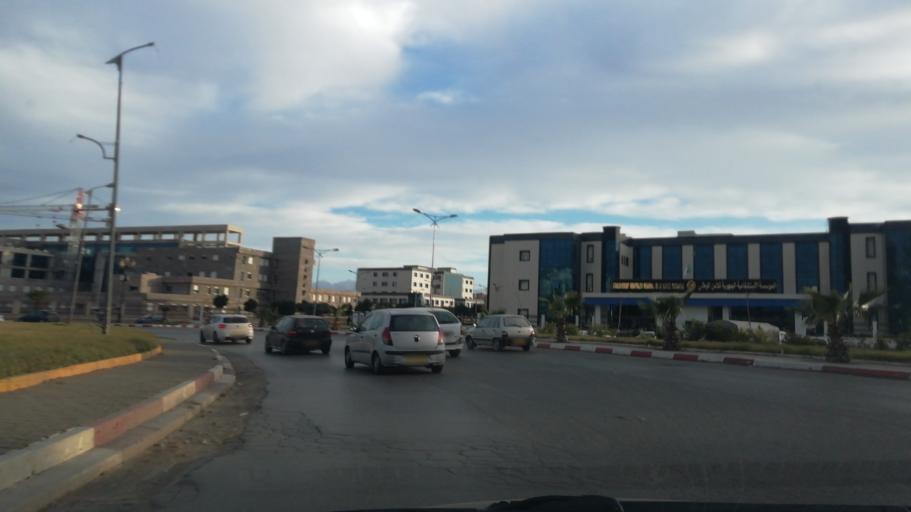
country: DZ
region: Oran
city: Bir el Djir
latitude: 35.6963
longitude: -0.5859
